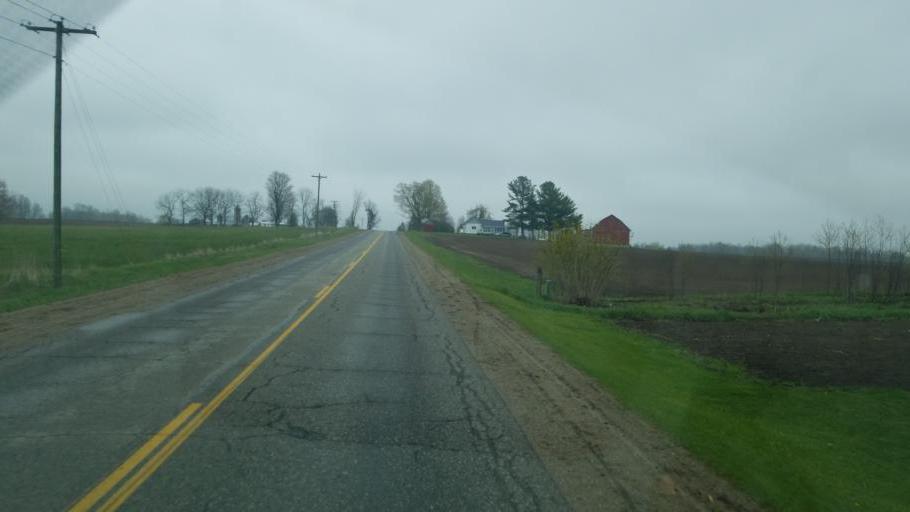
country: US
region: Michigan
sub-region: Mecosta County
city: Canadian Lakes
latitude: 43.5424
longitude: -85.3733
